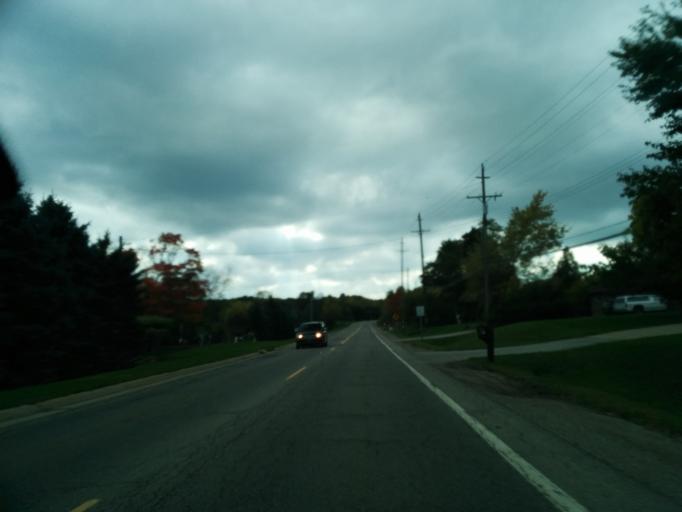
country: US
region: Michigan
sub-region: Oakland County
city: Waterford
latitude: 42.6991
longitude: -83.4612
